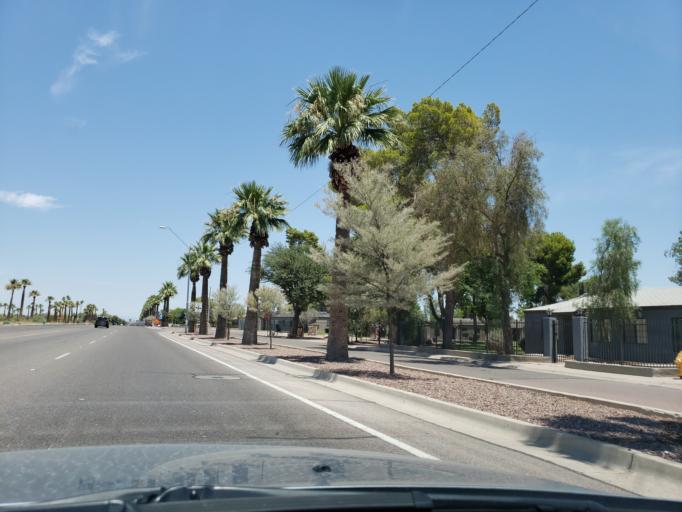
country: US
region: Arizona
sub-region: Maricopa County
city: Goodyear
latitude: 33.4415
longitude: -112.3582
